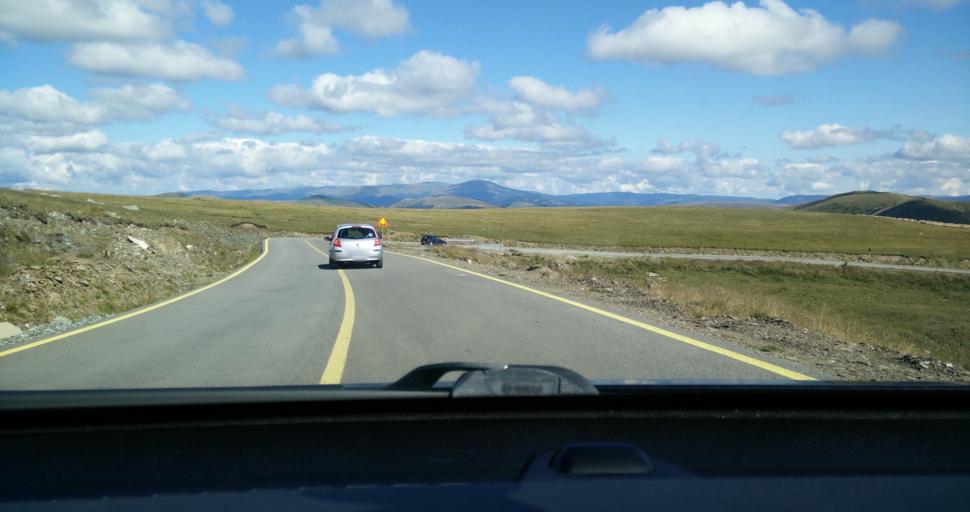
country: RO
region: Gorj
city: Novaci-Straini
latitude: 45.3679
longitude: 23.6510
